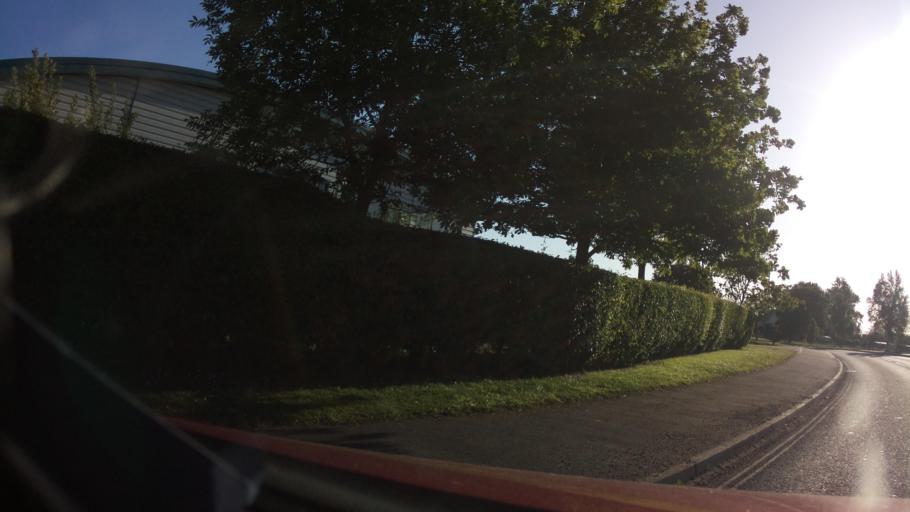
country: GB
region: England
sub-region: Devon
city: Topsham
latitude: 50.7297
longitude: -3.4122
